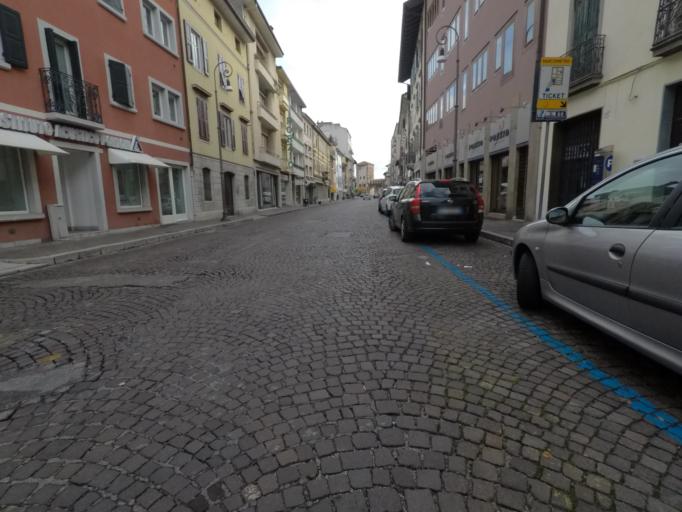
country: IT
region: Friuli Venezia Giulia
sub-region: Provincia di Udine
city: Udine
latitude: 46.0593
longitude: 13.2427
